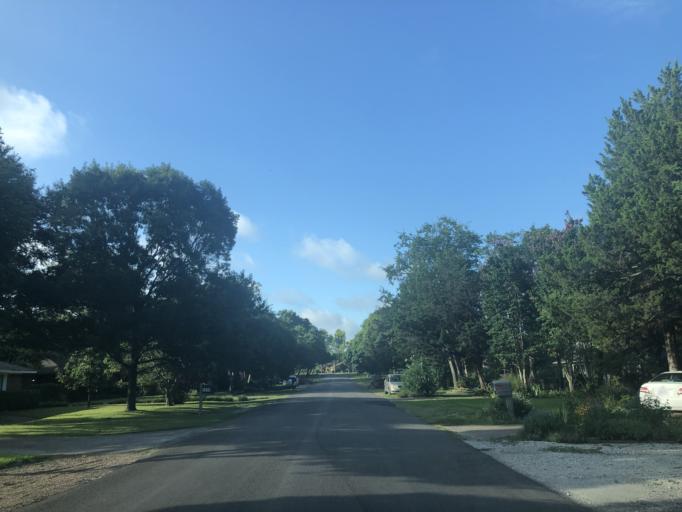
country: US
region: Texas
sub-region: Dallas County
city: Duncanville
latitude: 32.6723
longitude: -96.9196
